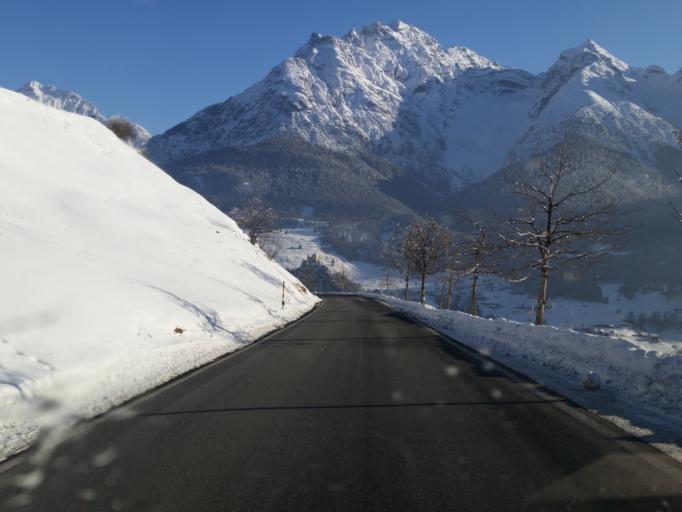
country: CH
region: Grisons
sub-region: Inn District
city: Scuol
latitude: 46.7933
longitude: 10.2503
